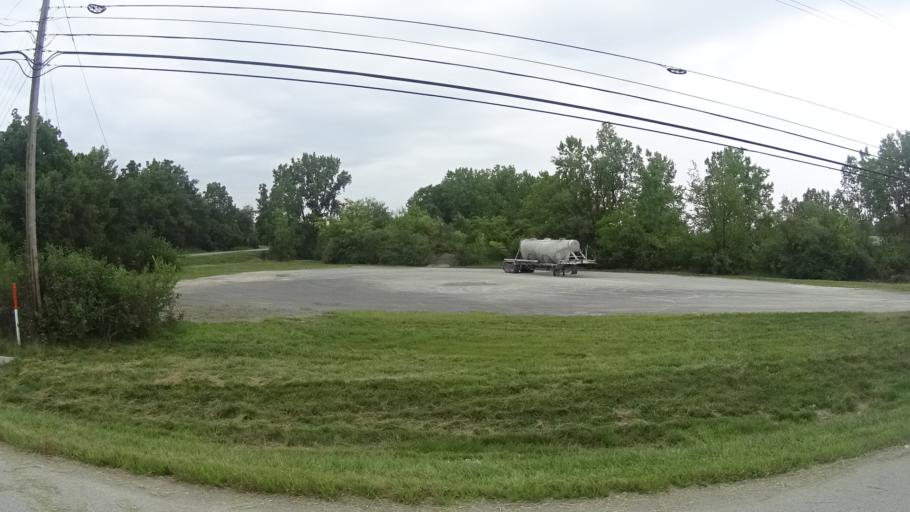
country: US
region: Indiana
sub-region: Madison County
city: Lapel
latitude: 40.0716
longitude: -85.8573
